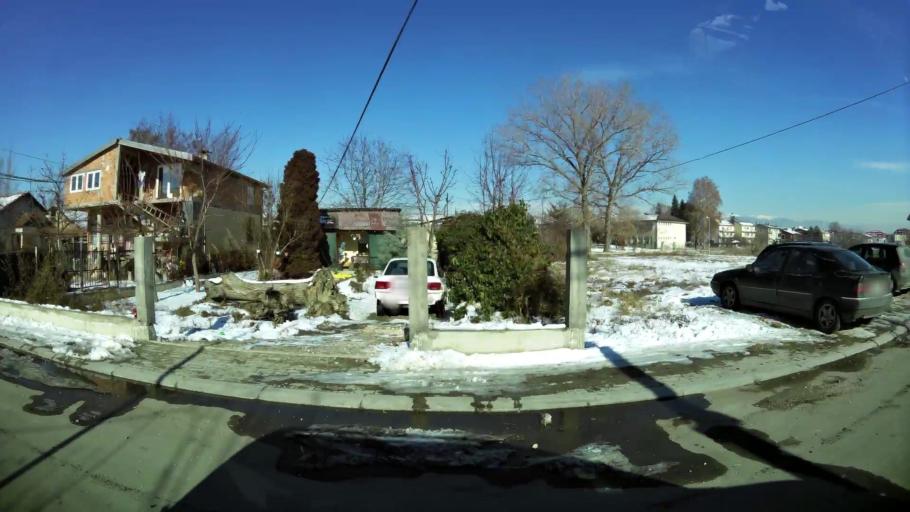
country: MK
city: Krushopek
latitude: 42.0020
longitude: 21.3568
